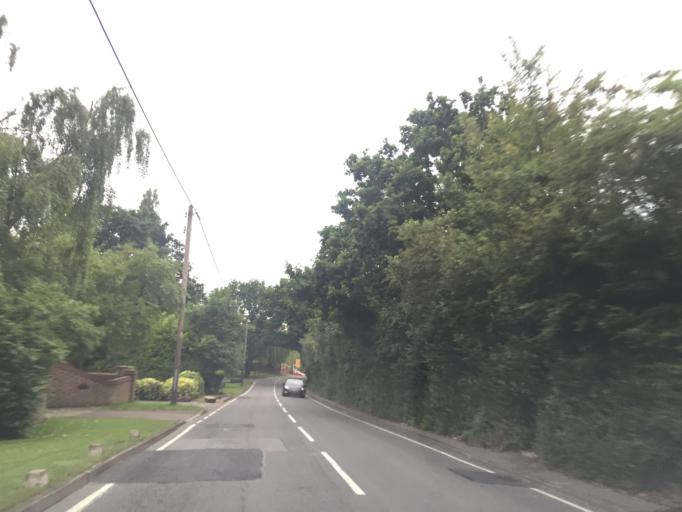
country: GB
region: England
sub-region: Greater London
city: Collier Row
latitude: 51.6303
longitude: 0.1779
